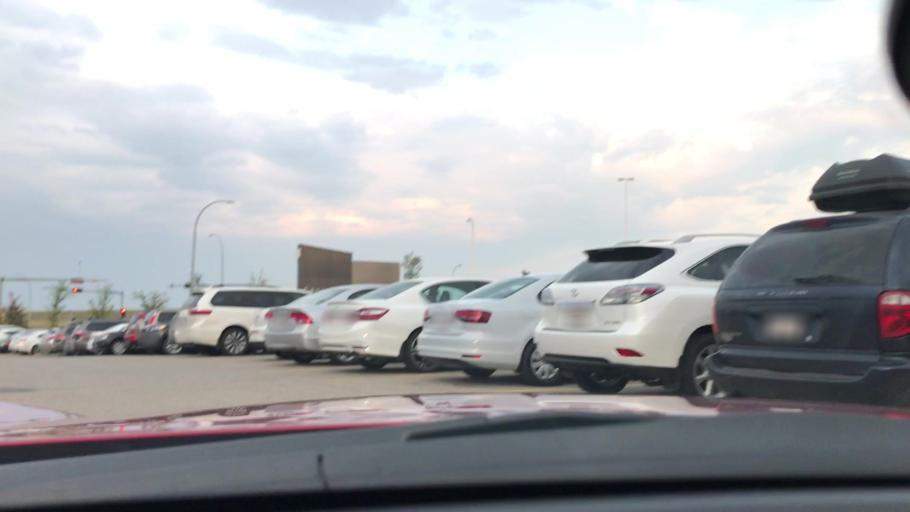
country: CA
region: Alberta
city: Airdrie
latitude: 51.2054
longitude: -113.9914
